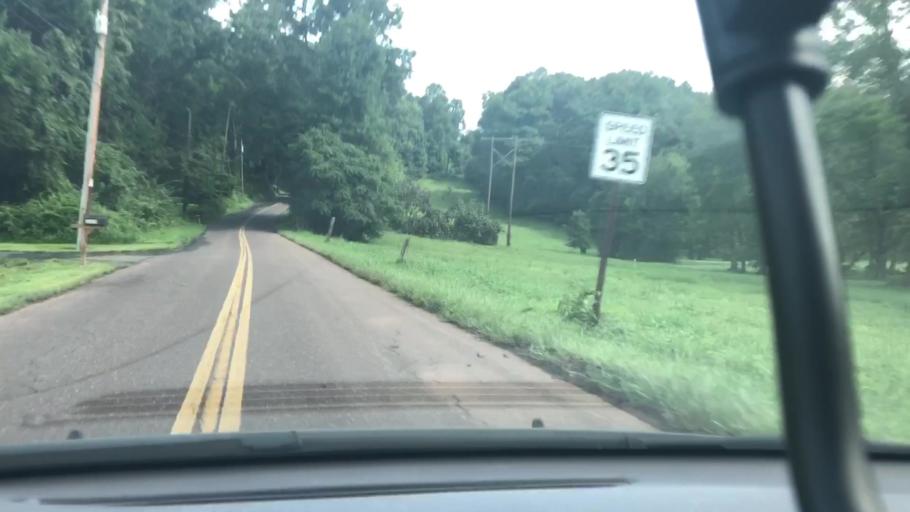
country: US
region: Pennsylvania
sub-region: Chester County
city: Kenilworth
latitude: 40.1909
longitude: -75.6470
